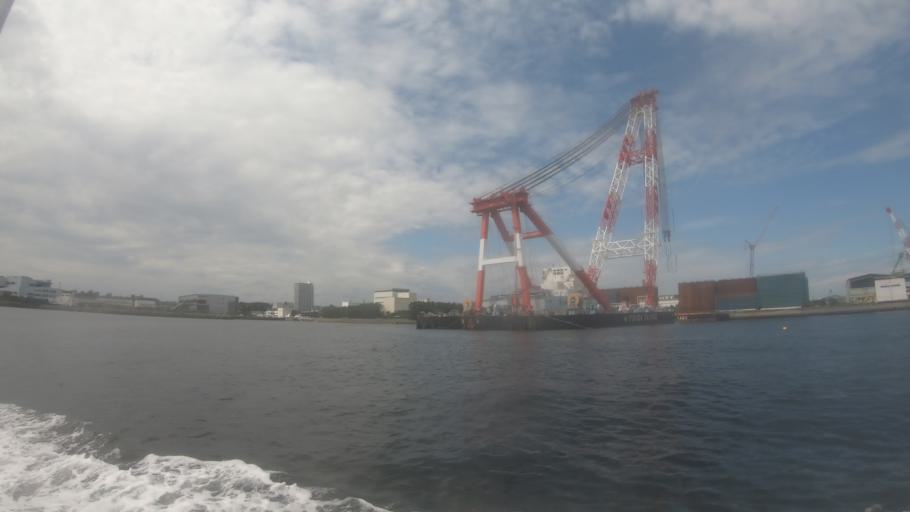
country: JP
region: Kanagawa
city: Yokohama
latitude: 35.3863
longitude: 139.6338
